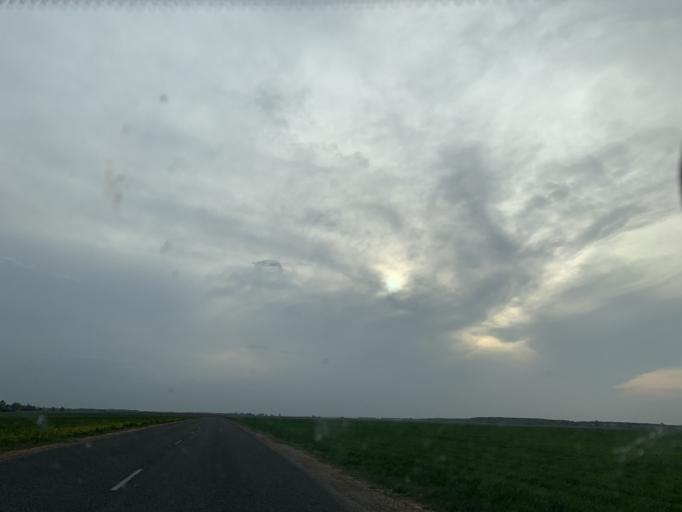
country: BY
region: Minsk
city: Kapyl'
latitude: 53.2908
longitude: 26.9993
